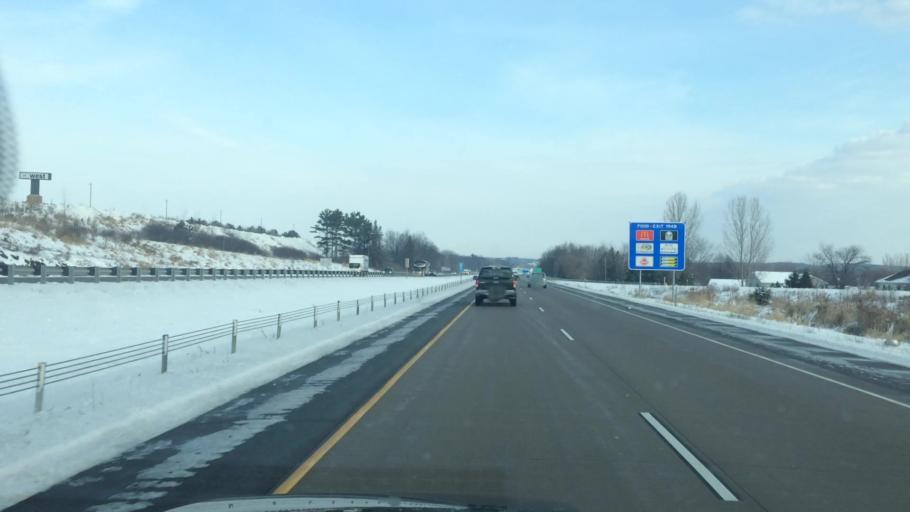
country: US
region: Wisconsin
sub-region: Marathon County
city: Wausau
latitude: 44.9707
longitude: -89.6562
